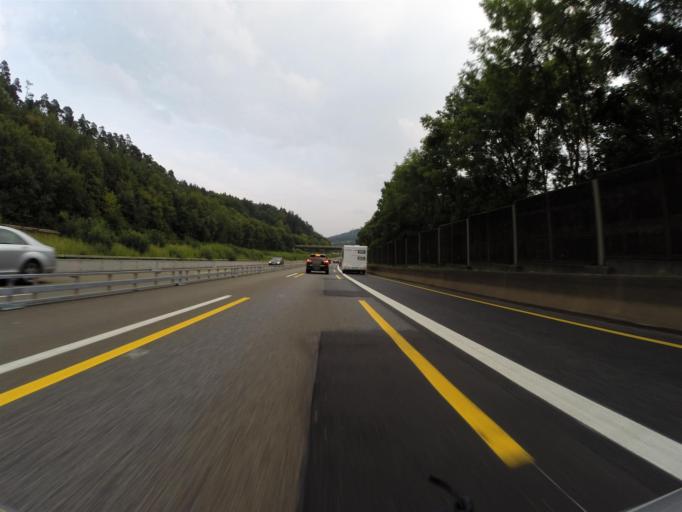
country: DE
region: Hesse
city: Schwarzenborn
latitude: 50.9850
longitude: 9.4718
